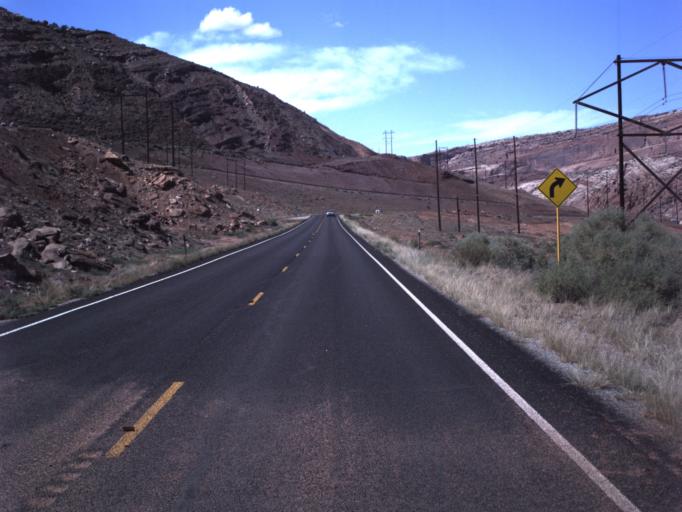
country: US
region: Utah
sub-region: Grand County
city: Moab
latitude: 38.5983
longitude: -109.6009
